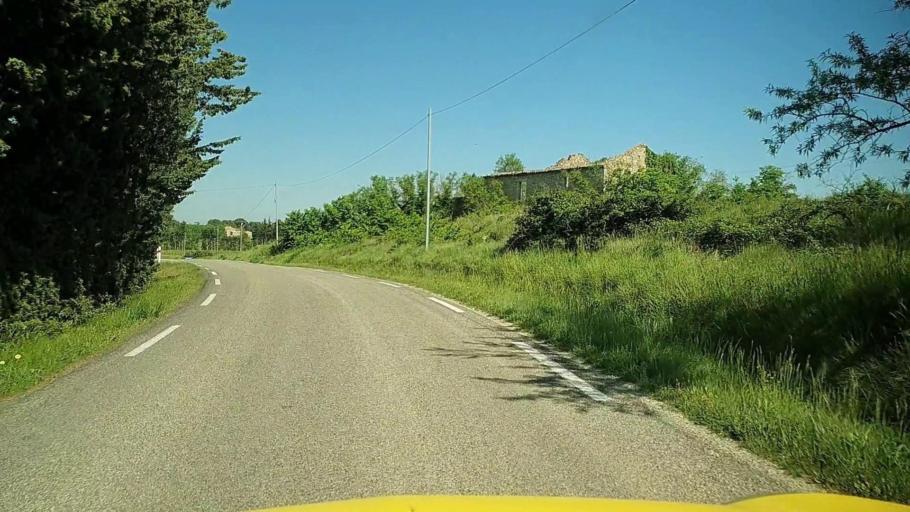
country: FR
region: Languedoc-Roussillon
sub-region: Departement du Gard
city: Saint-Chaptes
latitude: 43.9521
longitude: 4.3045
